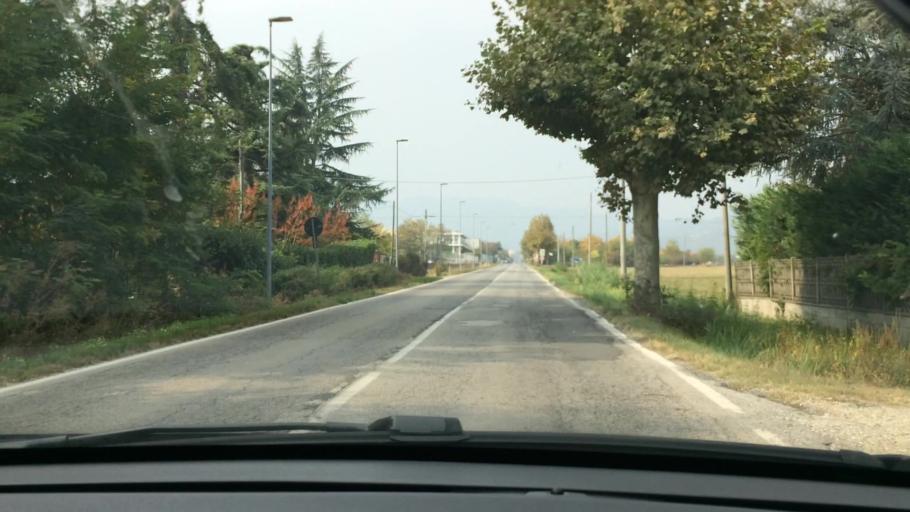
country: IT
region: Piedmont
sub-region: Provincia di Torino
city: Cumiana
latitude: 44.9635
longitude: 7.3986
